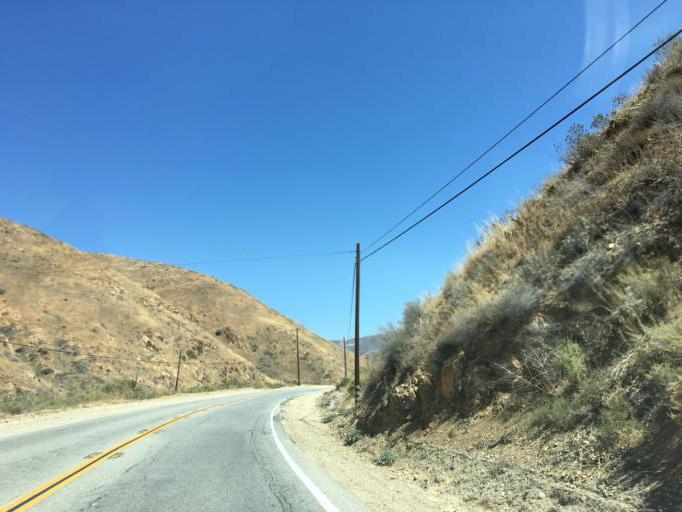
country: US
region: California
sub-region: Los Angeles County
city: Agua Dulce
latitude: 34.4854
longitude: -118.3886
